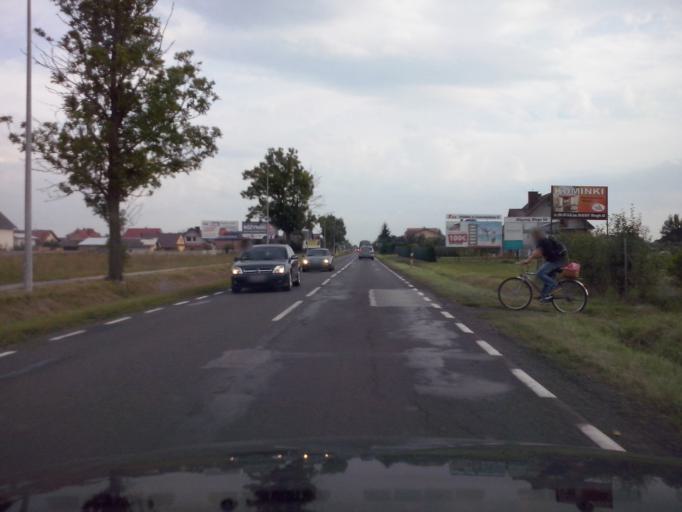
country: PL
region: Lublin Voivodeship
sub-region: Powiat bilgorajski
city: Bilgoraj
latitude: 50.5121
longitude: 22.7174
